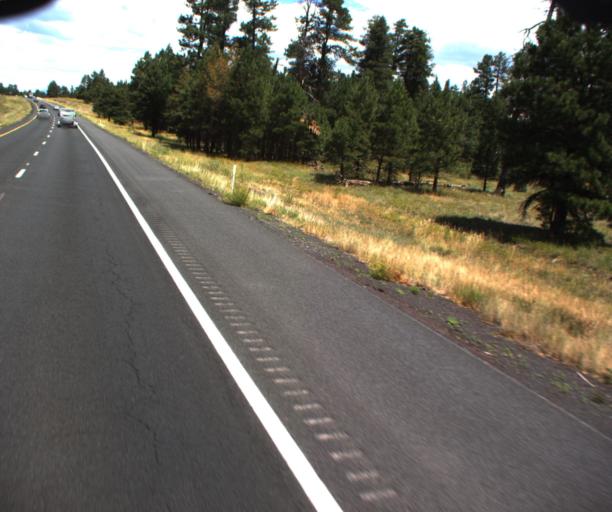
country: US
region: Arizona
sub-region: Coconino County
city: Sedona
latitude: 34.8967
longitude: -111.6412
